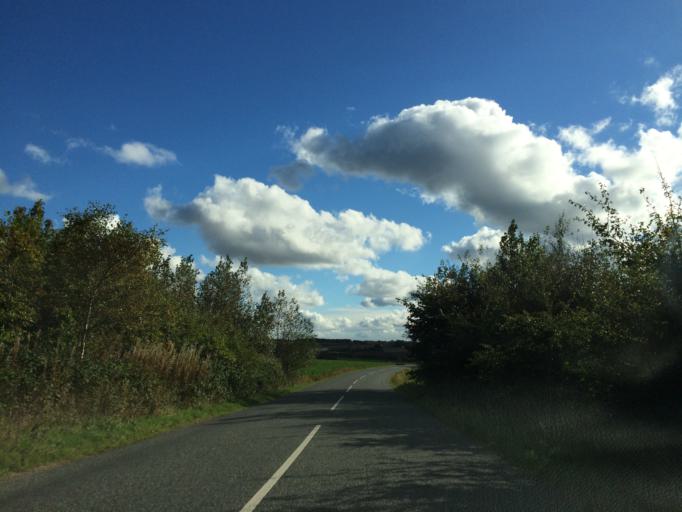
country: DK
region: Central Jutland
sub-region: Skanderborg Kommune
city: Ry
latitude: 56.1934
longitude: 9.7627
